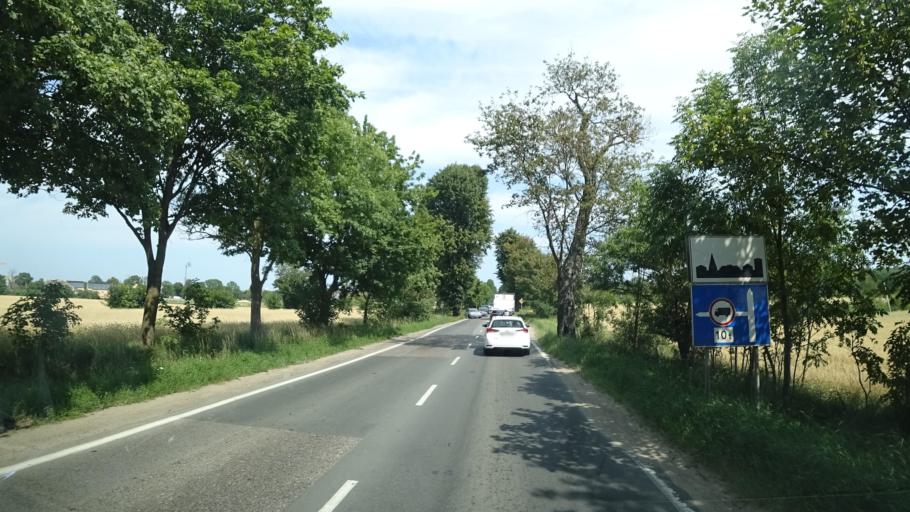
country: PL
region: Pomeranian Voivodeship
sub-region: Powiat gdanski
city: Lublewo Gdanskie
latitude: 54.3520
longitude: 18.4744
